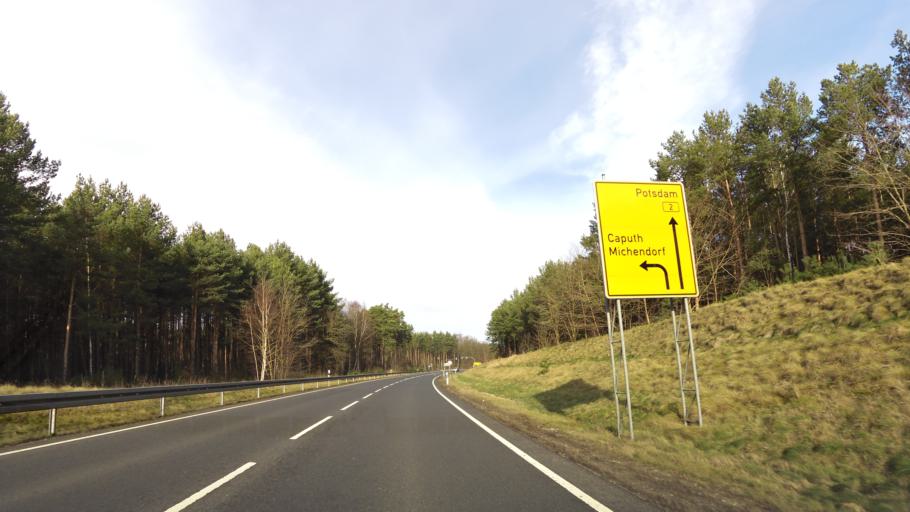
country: DE
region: Brandenburg
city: Michendorf
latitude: 52.3271
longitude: 13.0402
